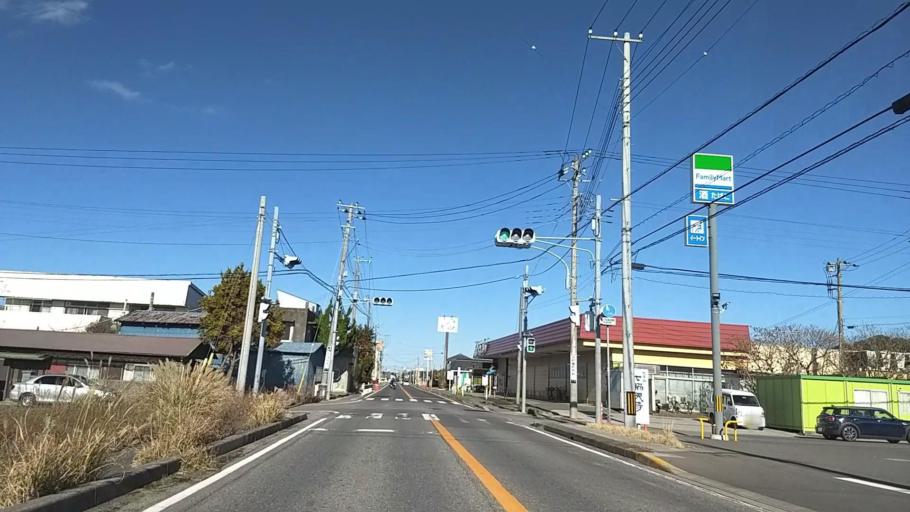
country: JP
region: Chiba
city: Ohara
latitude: 35.2400
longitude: 140.3916
